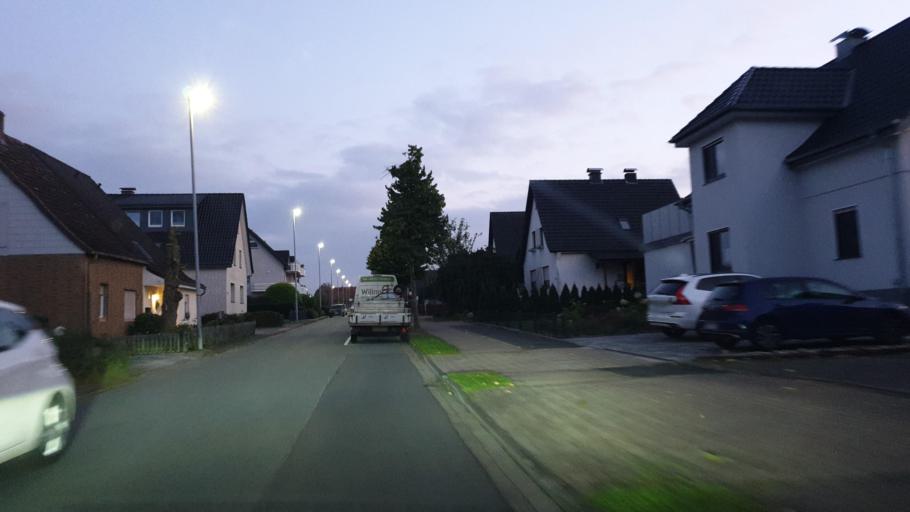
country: DE
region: North Rhine-Westphalia
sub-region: Regierungsbezirk Detmold
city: Hiddenhausen
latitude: 52.1592
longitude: 8.6345
